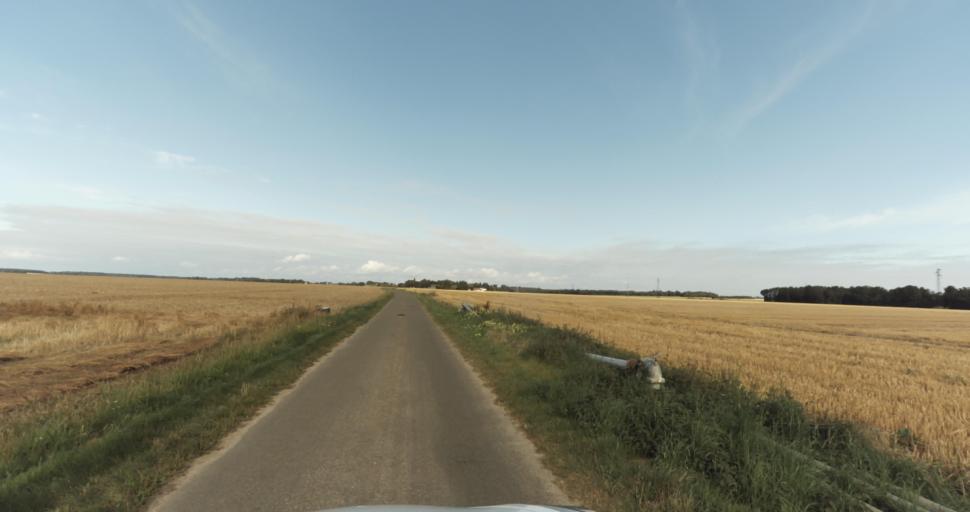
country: FR
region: Haute-Normandie
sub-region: Departement de l'Eure
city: Nonancourt
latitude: 48.8230
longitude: 1.1567
